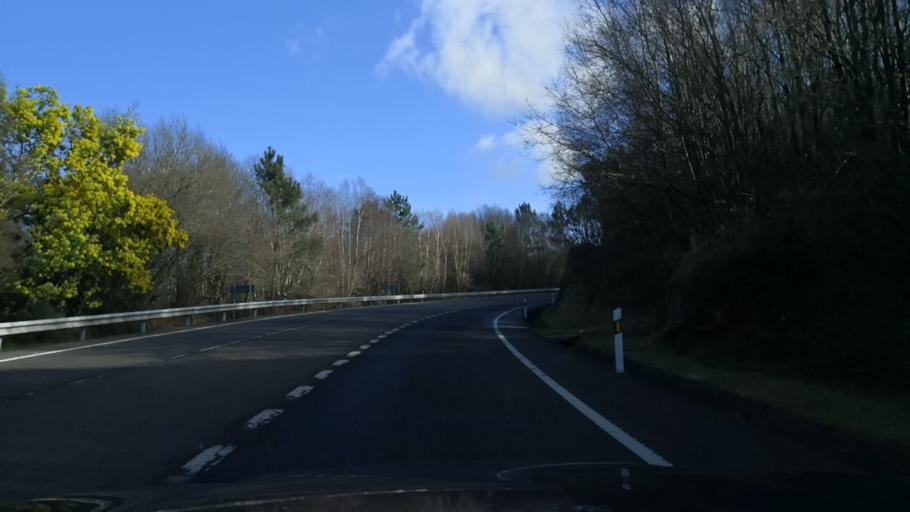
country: ES
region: Galicia
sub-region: Provincia da Coruna
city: Ribeira
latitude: 42.7146
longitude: -8.3609
